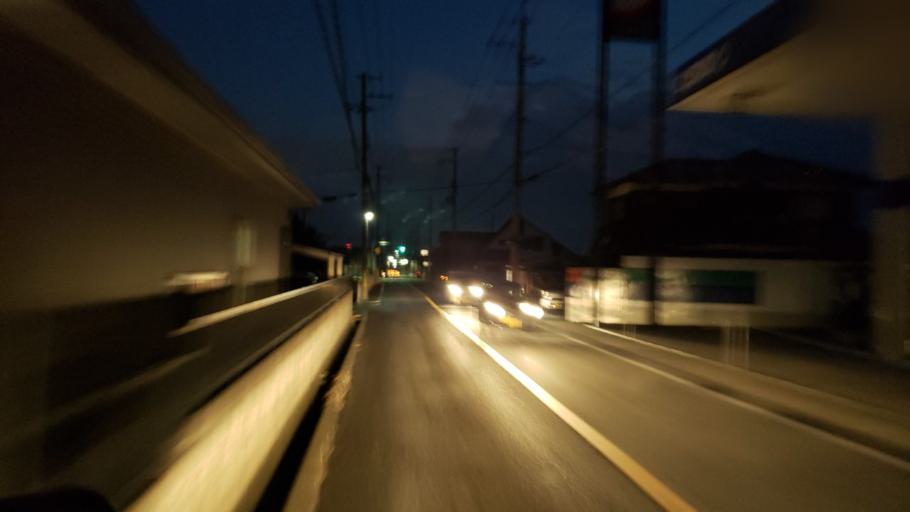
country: JP
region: Hyogo
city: Kakogawacho-honmachi
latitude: 34.8070
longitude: 134.8185
